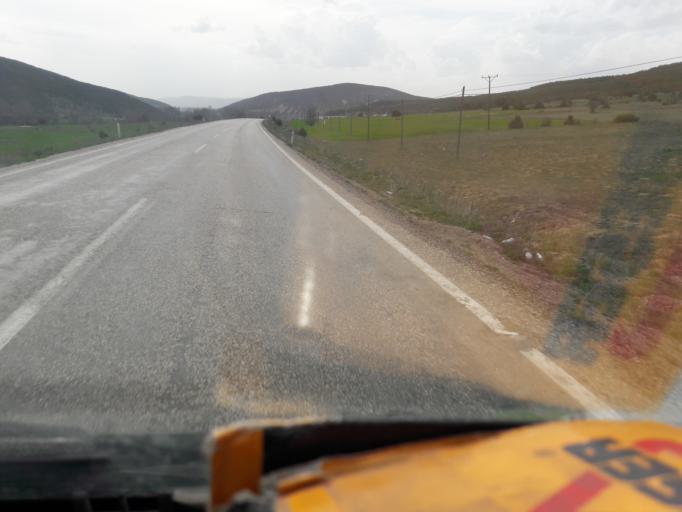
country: TR
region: Gumushane
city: Siran
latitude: 40.1729
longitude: 39.1671
